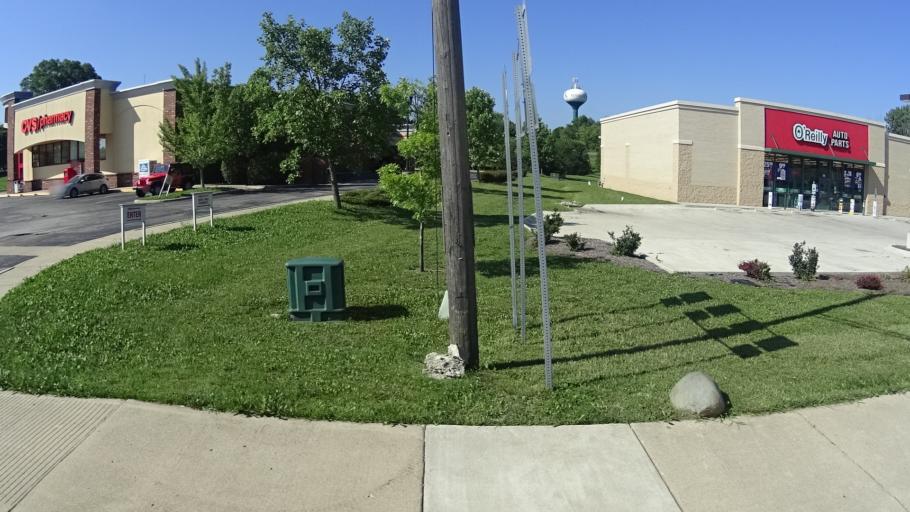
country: US
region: Indiana
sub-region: Madison County
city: Pendleton
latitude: 40.0001
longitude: -85.7364
